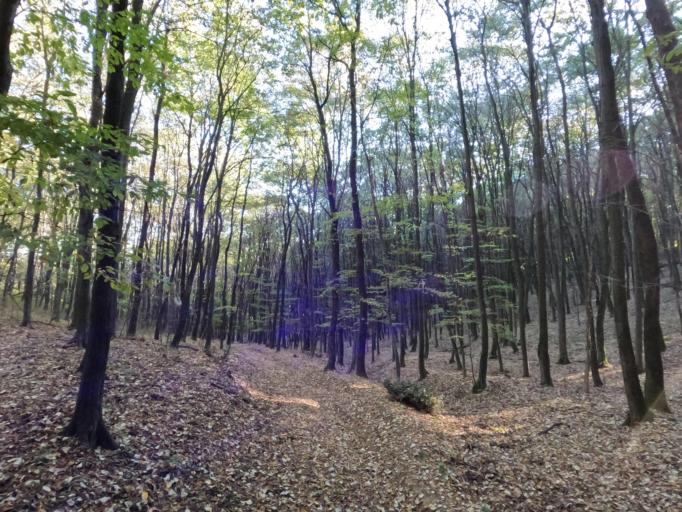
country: HU
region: Tolna
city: Szekszard
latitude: 46.3109
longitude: 18.6527
